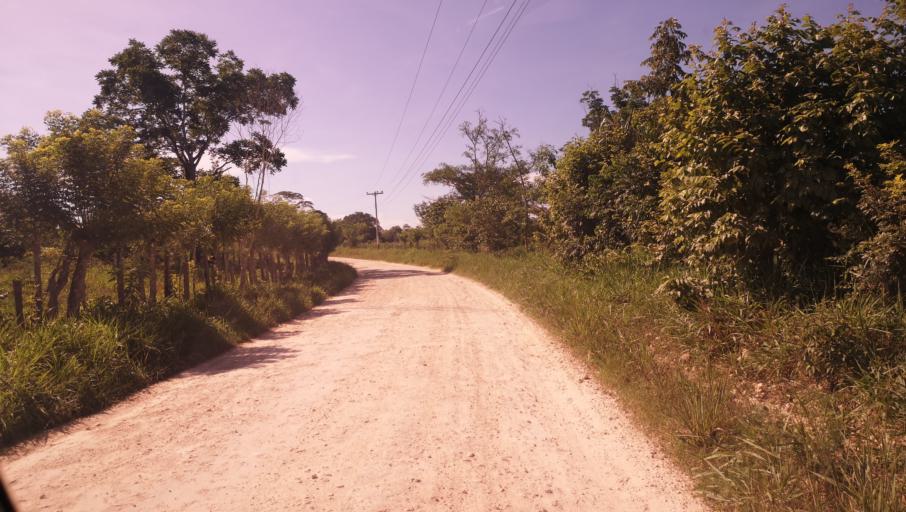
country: GT
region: Peten
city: Dolores
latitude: 16.7153
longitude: -89.3676
